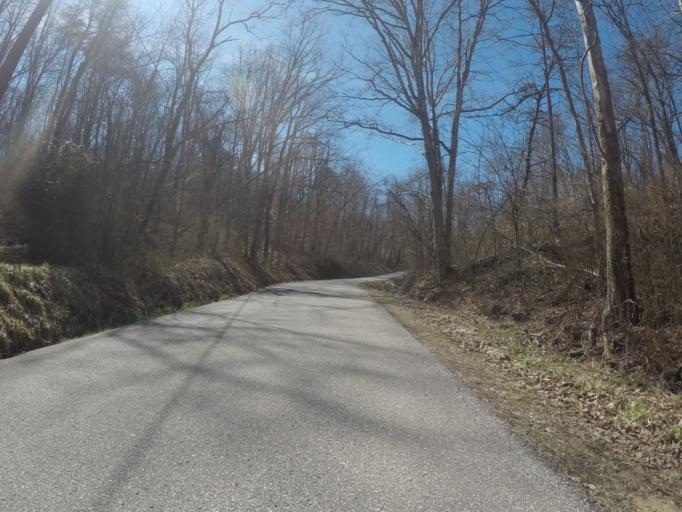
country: US
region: Ohio
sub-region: Lawrence County
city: South Point
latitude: 38.4843
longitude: -82.5665
